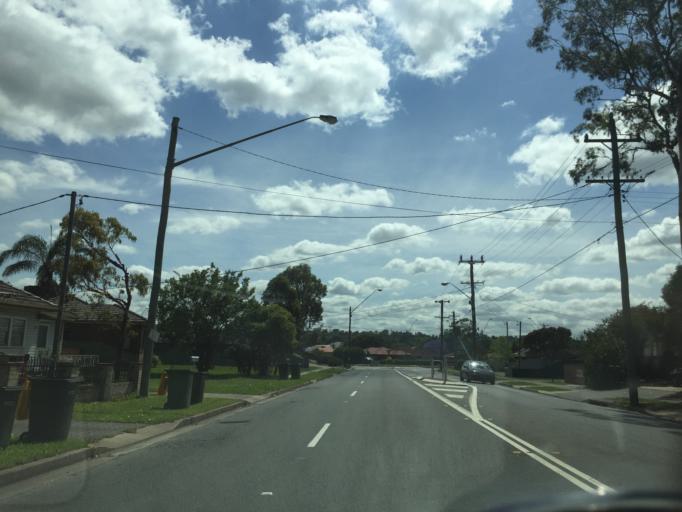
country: AU
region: New South Wales
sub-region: Holroyd
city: Girraween
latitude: -33.7848
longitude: 150.9532
